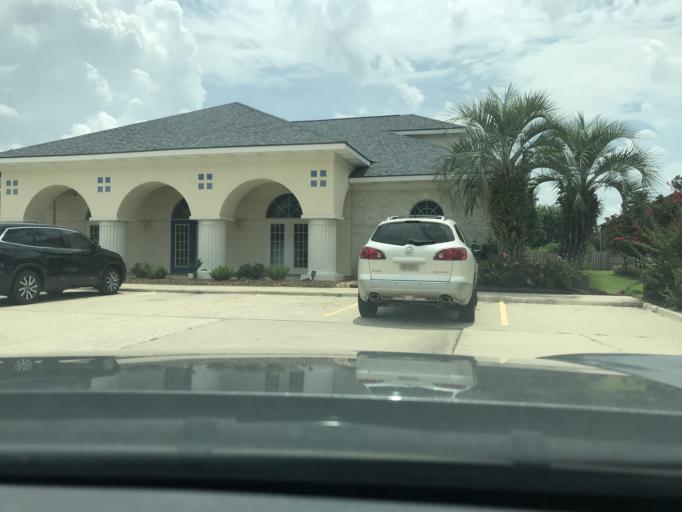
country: US
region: Louisiana
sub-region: Calcasieu Parish
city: Sulphur
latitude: 30.2274
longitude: -93.3407
